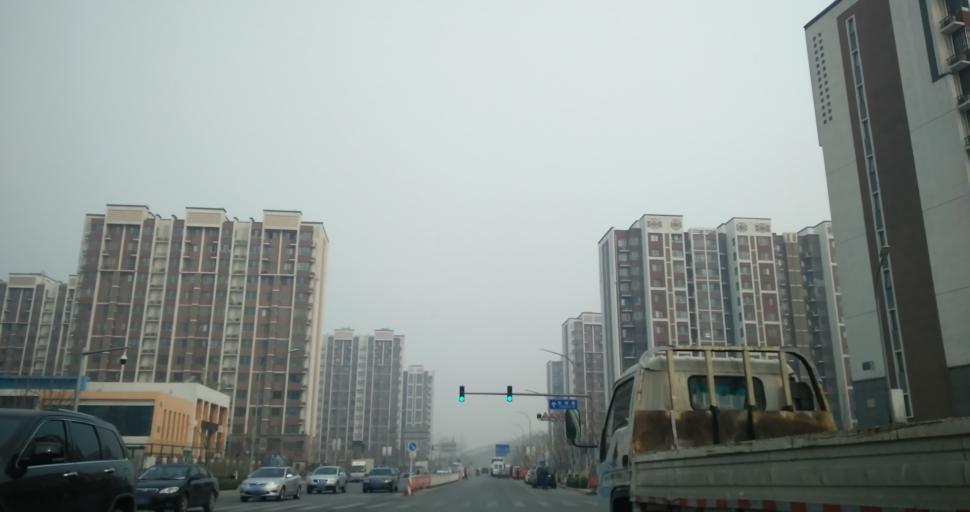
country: CN
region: Beijing
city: Yinghai
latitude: 39.7607
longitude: 116.4300
